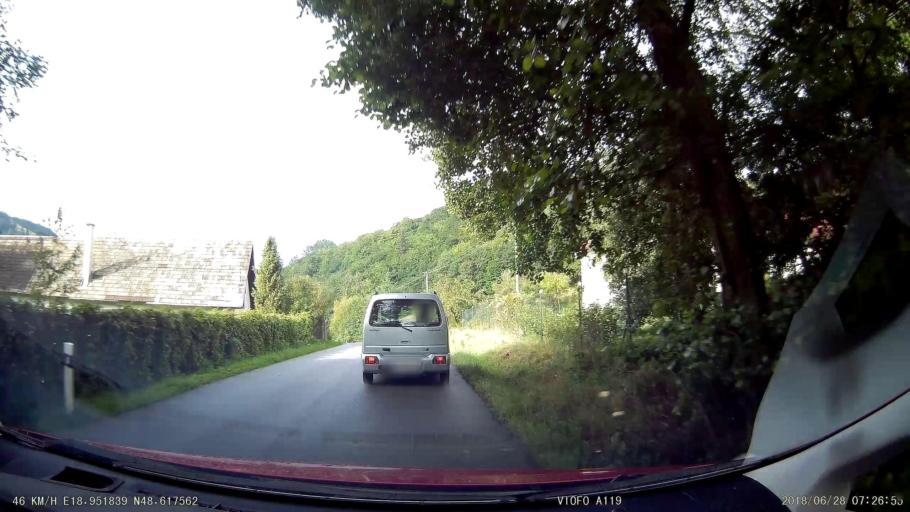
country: SK
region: Banskobystricky
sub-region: Okres Ziar nad Hronom
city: Kremnica
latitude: 48.6173
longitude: 18.9517
